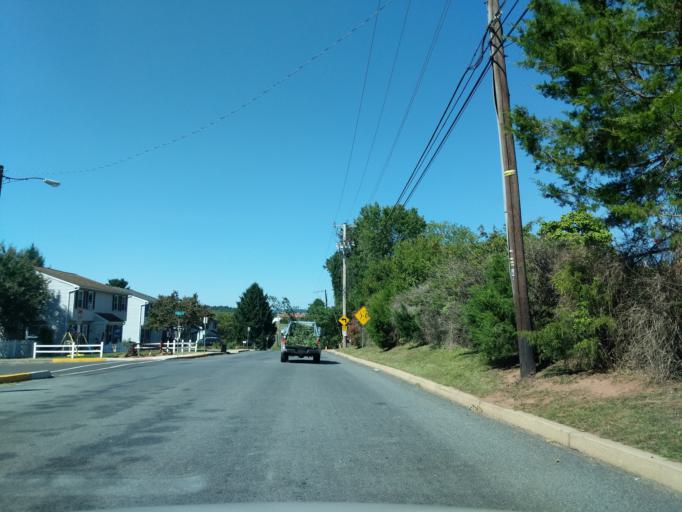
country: US
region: Pennsylvania
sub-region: Montgomery County
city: East Greenville
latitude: 40.4065
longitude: -75.5105
